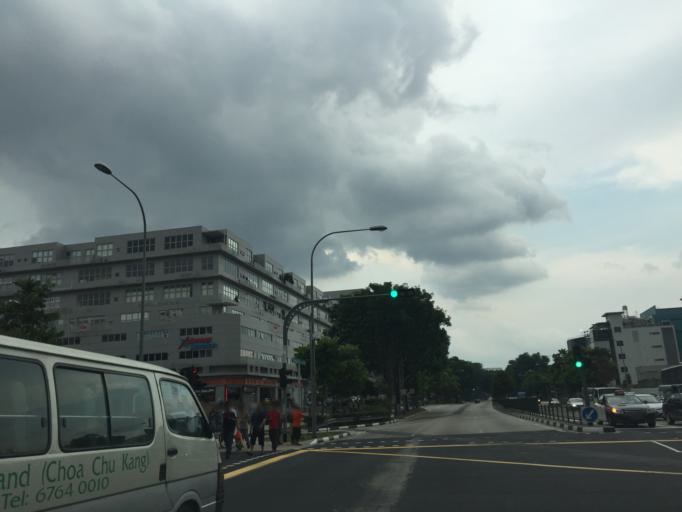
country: MY
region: Johor
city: Johor Bahru
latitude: 1.3348
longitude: 103.6966
